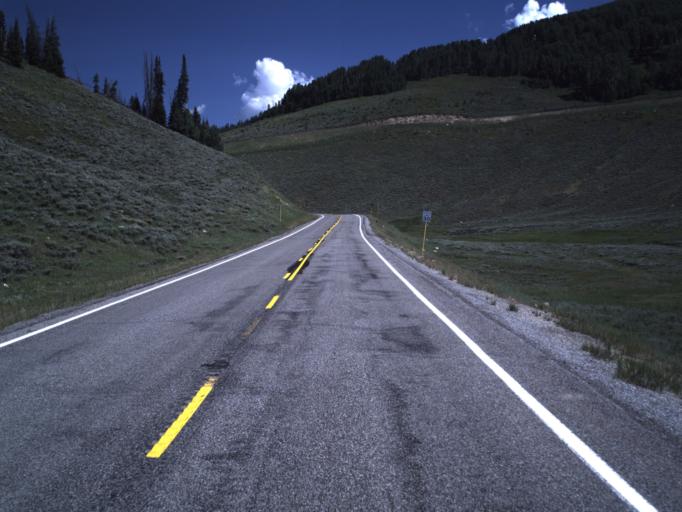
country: US
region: Utah
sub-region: Sanpete County
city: Fairview
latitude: 39.6782
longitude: -111.2435
